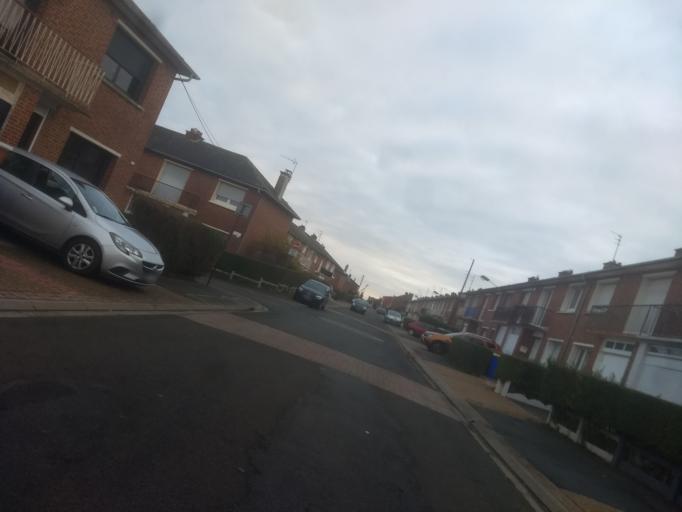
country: FR
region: Nord-Pas-de-Calais
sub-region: Departement du Pas-de-Calais
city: Anzin-Saint-Aubin
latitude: 50.2964
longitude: 2.7457
